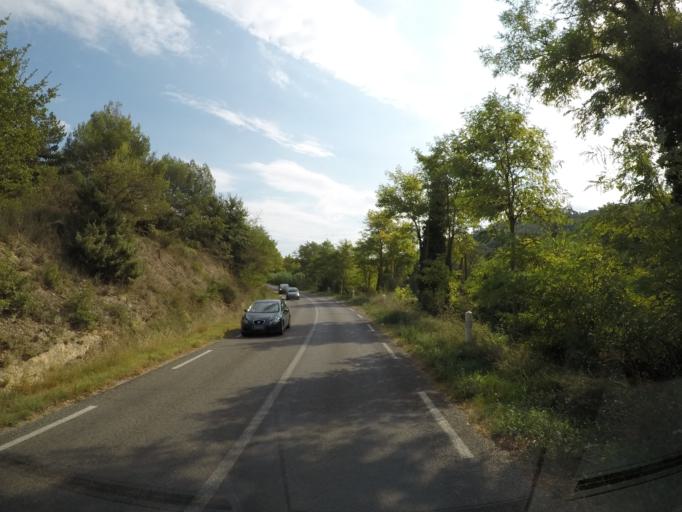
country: FR
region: Provence-Alpes-Cote d'Azur
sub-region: Departement du Vaucluse
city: Ansouis
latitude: 43.7368
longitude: 5.4706
